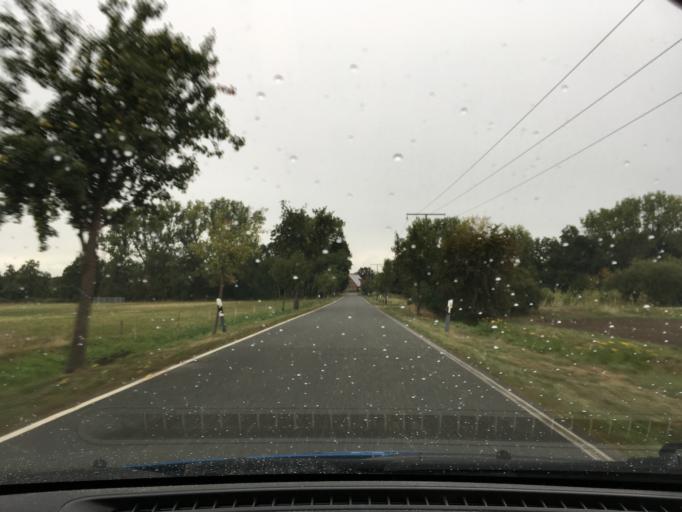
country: DE
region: Lower Saxony
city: Hitzacker
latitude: 53.2226
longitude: 10.9880
